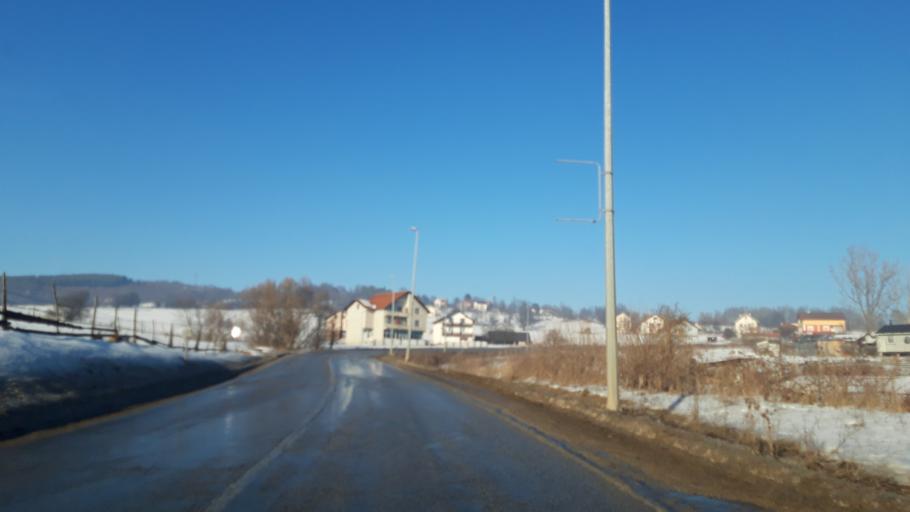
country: BA
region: Republika Srpska
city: Sokolac
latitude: 43.9216
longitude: 18.7742
